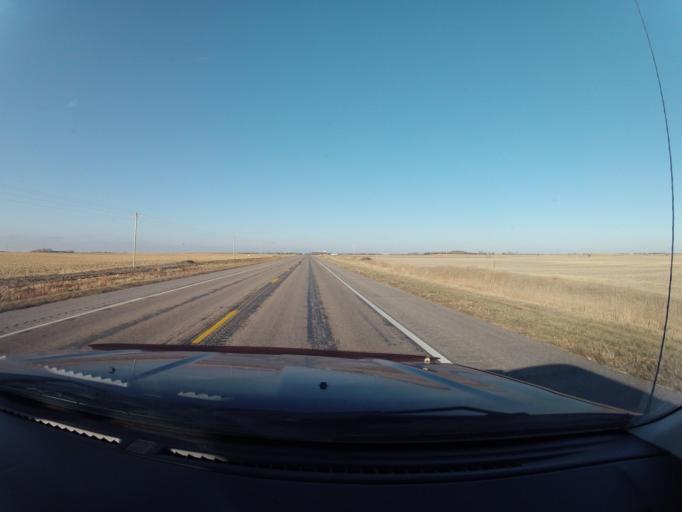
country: US
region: Nebraska
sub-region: Kearney County
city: Minden
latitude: 40.5803
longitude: -98.9518
